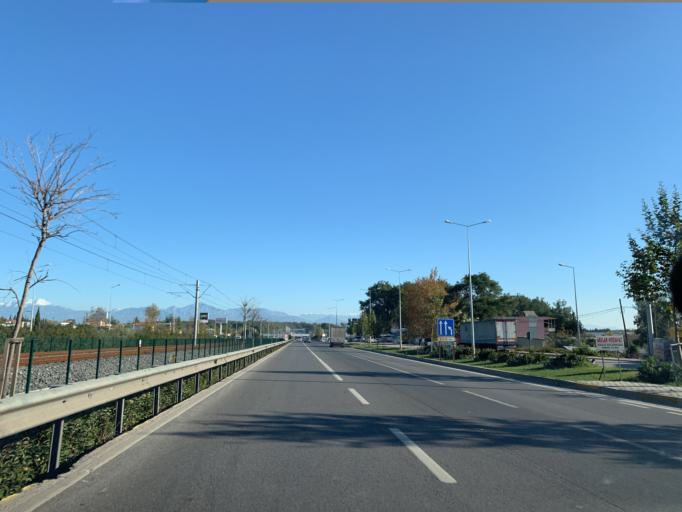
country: TR
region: Antalya
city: Aksu
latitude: 36.9396
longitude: 30.8217
